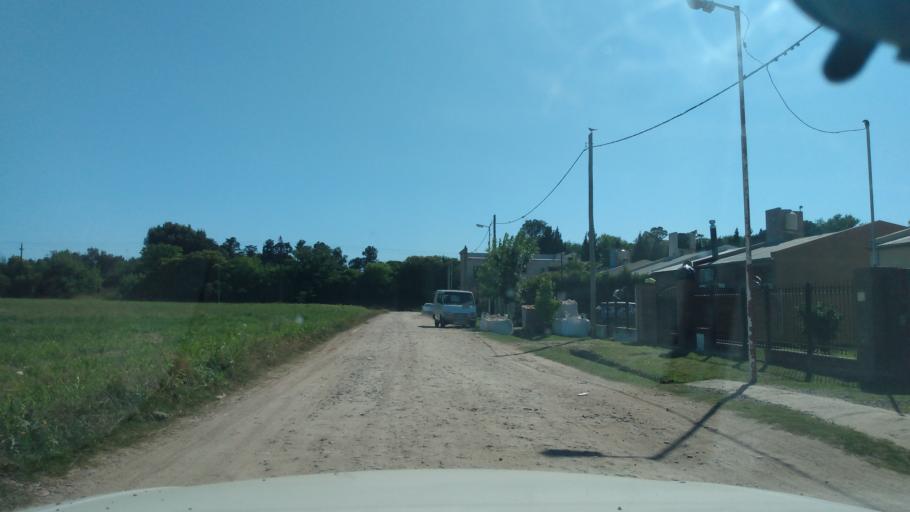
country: AR
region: Buenos Aires
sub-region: Partido de Lujan
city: Lujan
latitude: -34.5528
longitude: -59.1353
